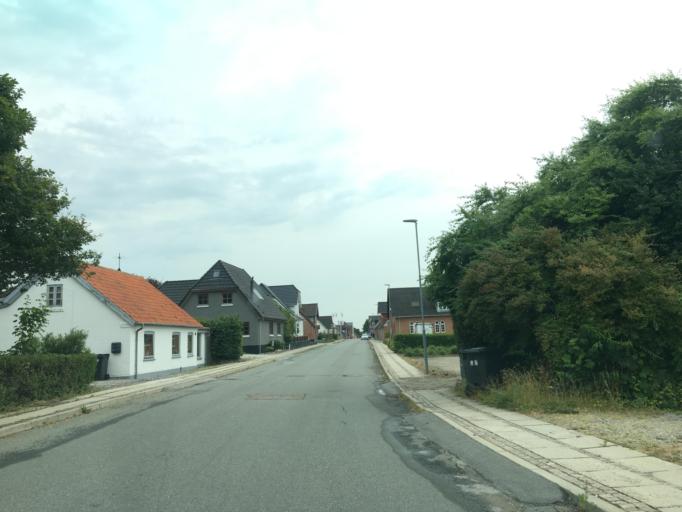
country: DK
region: North Denmark
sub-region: Thisted Kommune
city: Hurup
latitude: 56.8100
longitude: 8.4032
